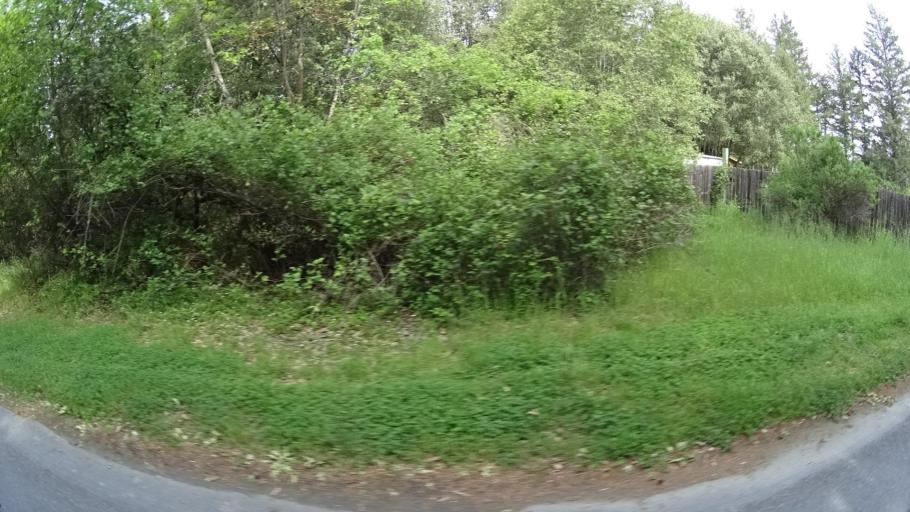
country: US
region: California
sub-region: Humboldt County
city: Redway
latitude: 40.0926
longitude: -123.8045
